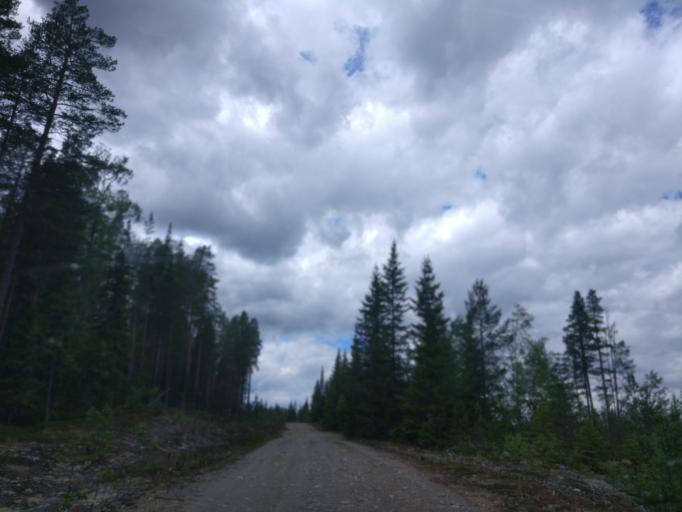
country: SE
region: Jaemtland
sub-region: Harjedalens Kommun
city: Sveg
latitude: 62.1981
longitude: 13.4091
